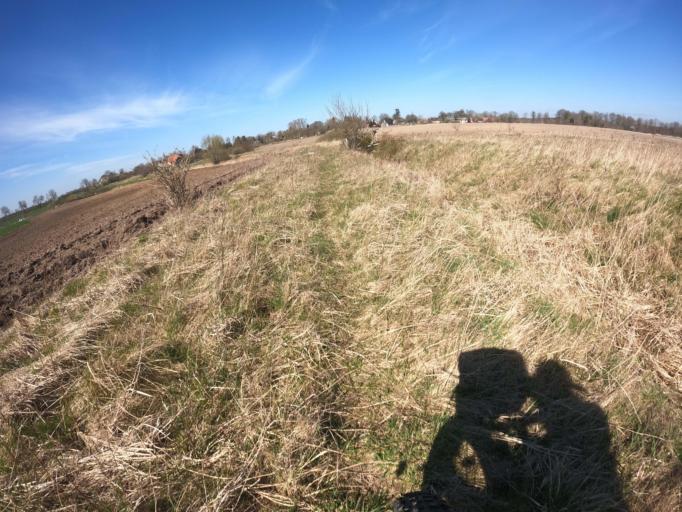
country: PL
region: West Pomeranian Voivodeship
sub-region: Powiat gryficki
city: Brojce
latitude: 53.9957
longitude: 15.3839
